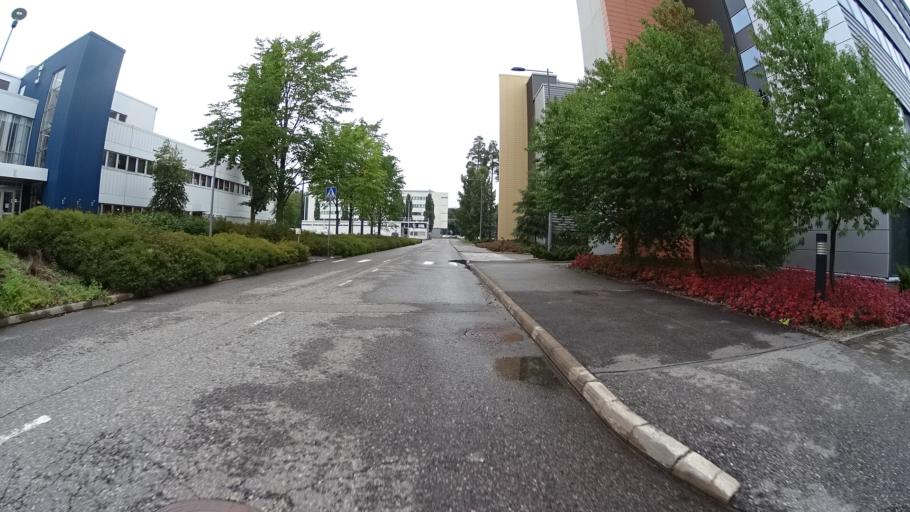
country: FI
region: Uusimaa
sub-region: Helsinki
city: Kilo
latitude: 60.2222
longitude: 24.7550
